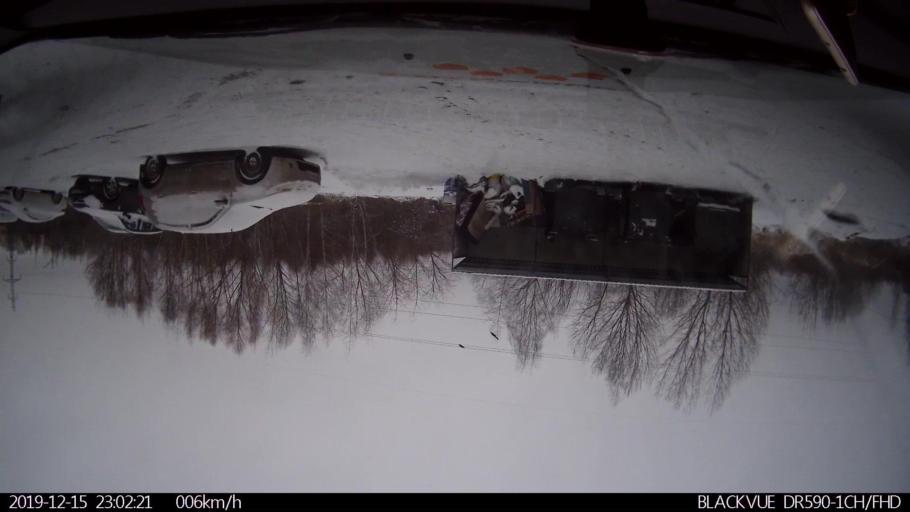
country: RU
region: Nizjnij Novgorod
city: Nizhniy Novgorod
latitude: 56.3381
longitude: 43.9122
